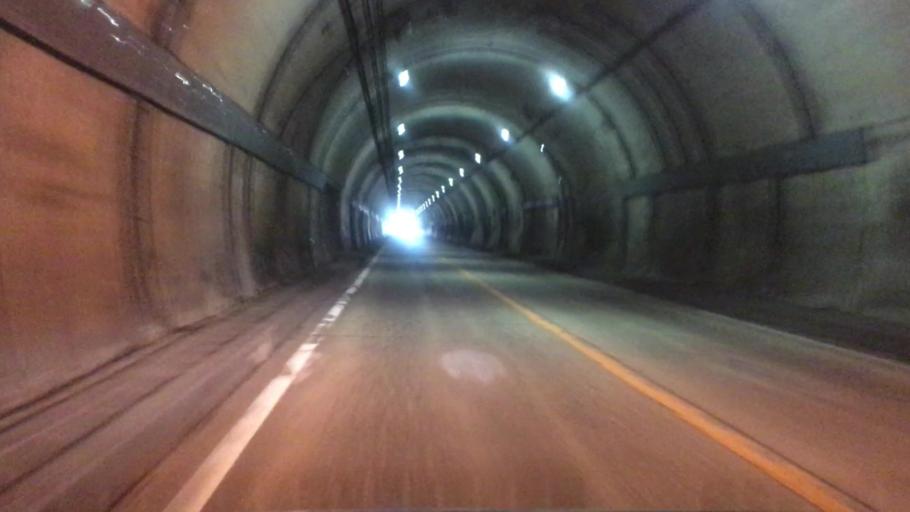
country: JP
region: Hyogo
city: Toyooka
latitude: 35.5834
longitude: 134.8613
